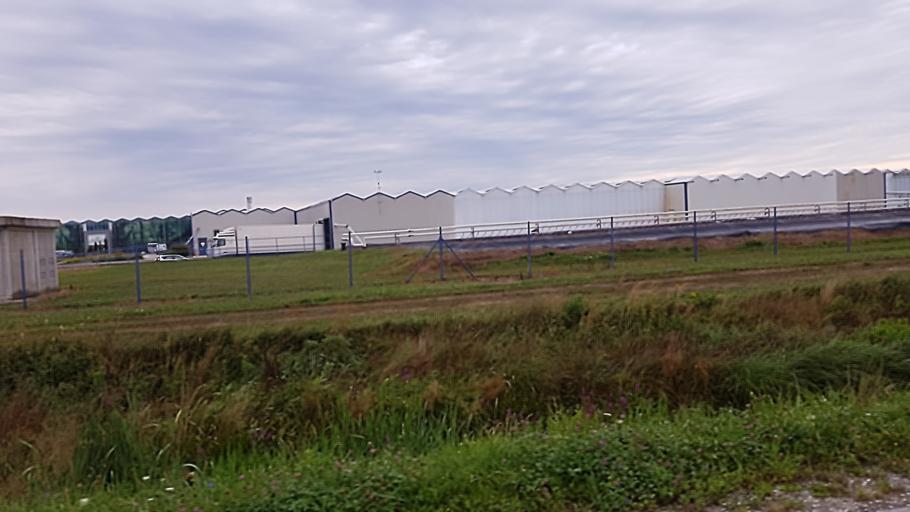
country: SI
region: Dobrovnik-Dobronak
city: Dobrovnik
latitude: 46.6373
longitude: 16.3455
